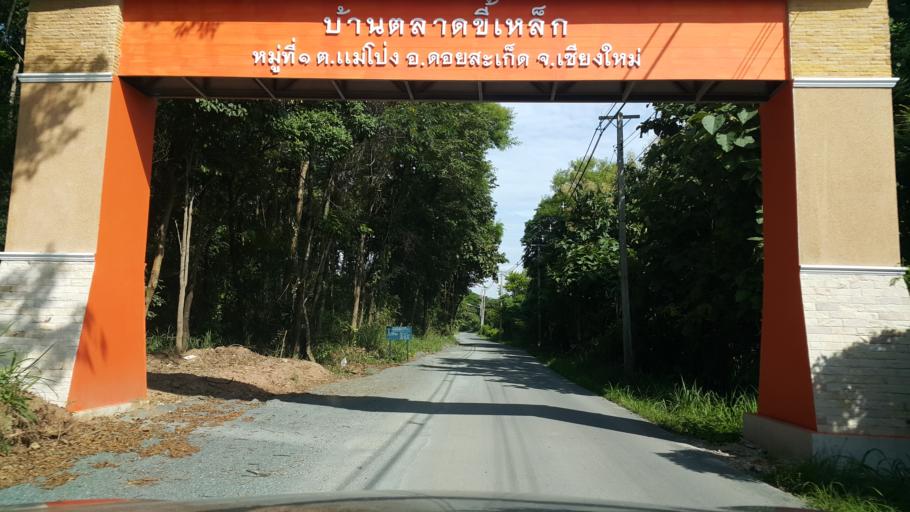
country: TH
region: Chiang Mai
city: Mae On
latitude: 18.8334
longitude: 99.1965
